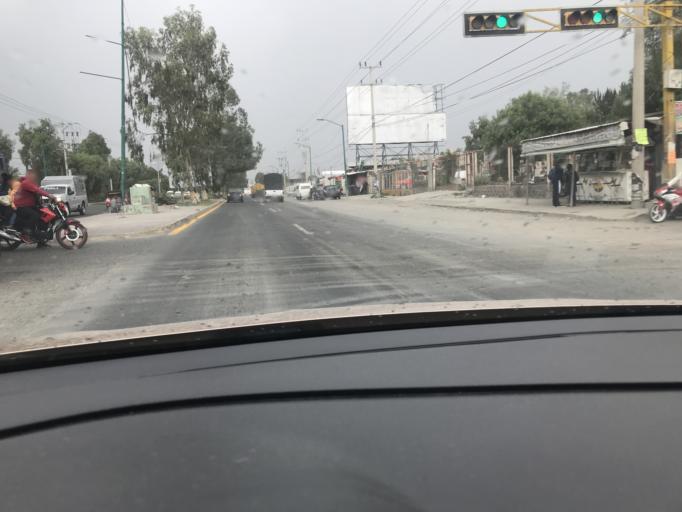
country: MX
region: Mexico
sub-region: La Paz
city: Arenal
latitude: 19.3859
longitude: -98.9378
